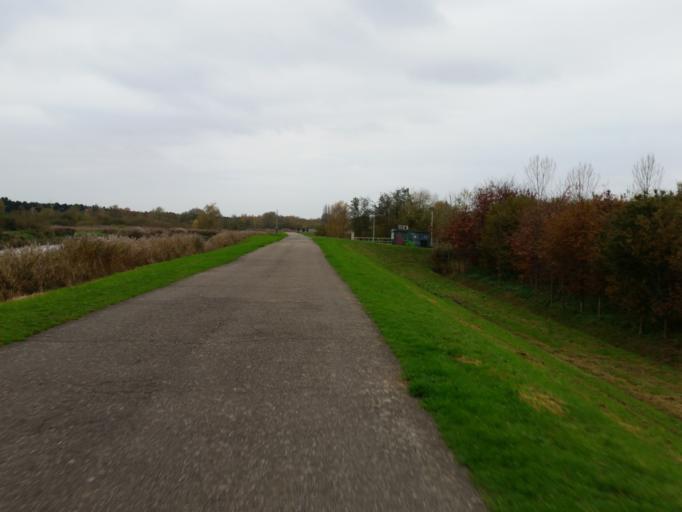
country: BE
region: Flanders
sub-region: Provincie Antwerpen
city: Lier
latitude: 51.1154
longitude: 4.5447
